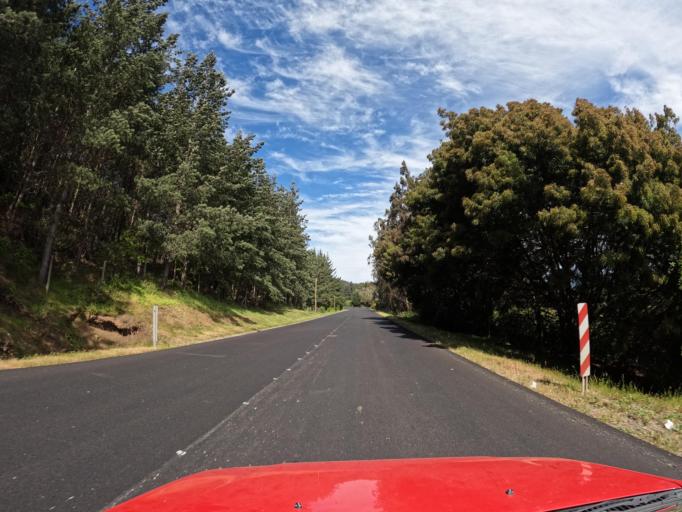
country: CL
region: Maule
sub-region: Provincia de Talca
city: Constitucion
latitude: -35.0484
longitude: -72.0482
